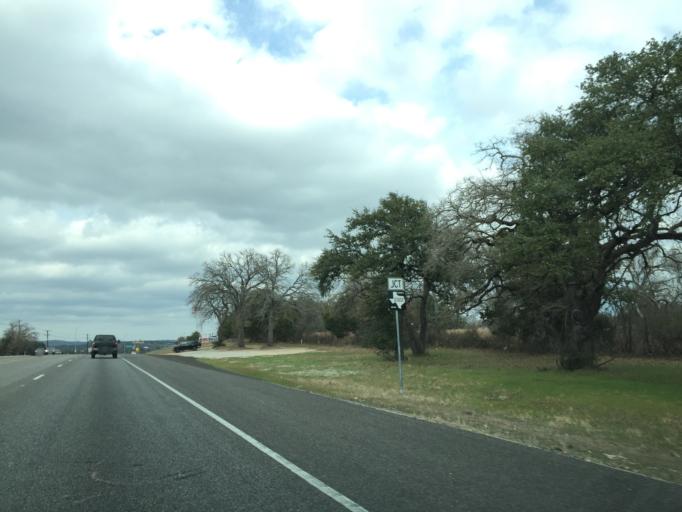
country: US
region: Texas
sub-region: Travis County
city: Briarcliff
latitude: 30.3825
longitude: -98.0842
